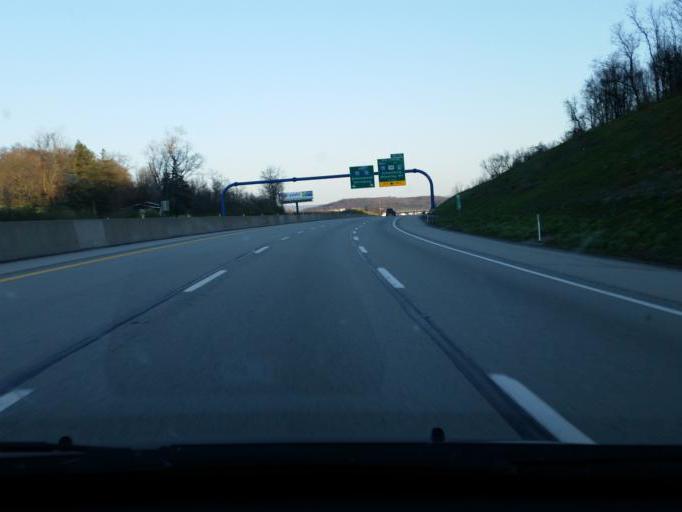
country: US
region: Pennsylvania
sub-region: Westmoreland County
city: New Stanton
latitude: 40.2383
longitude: -79.6241
